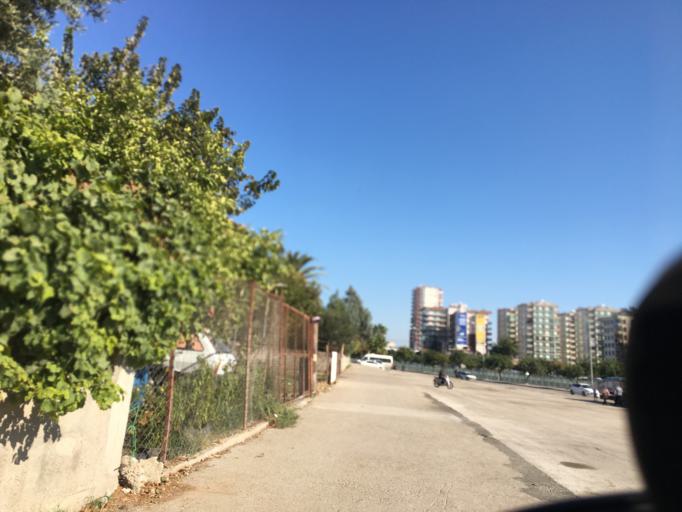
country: TR
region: Adana
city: Seyhan
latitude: 37.0112
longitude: 35.3006
